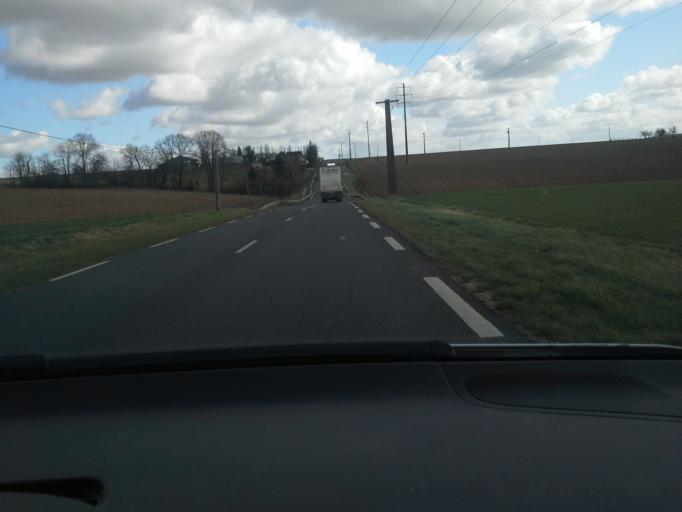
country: FR
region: Centre
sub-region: Departement du Loir-et-Cher
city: Moree
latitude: 47.9043
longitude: 1.2683
